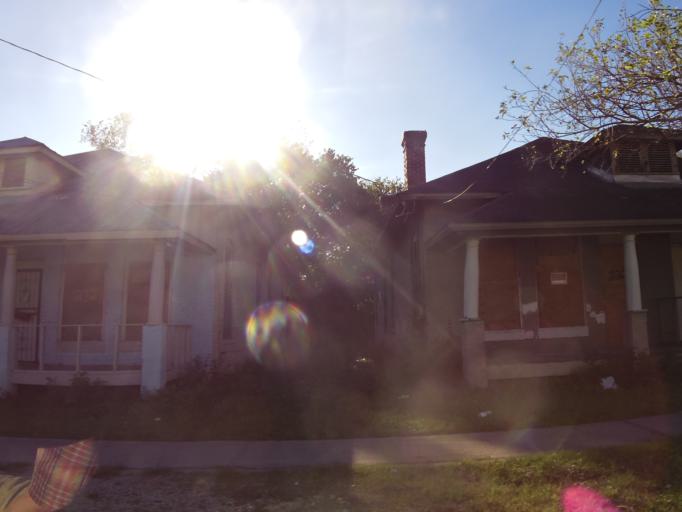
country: US
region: Florida
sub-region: Duval County
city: Jacksonville
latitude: 30.3523
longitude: -81.6708
